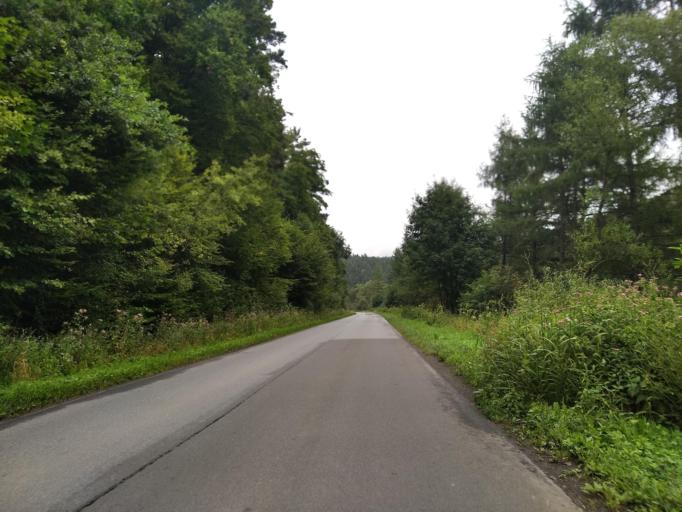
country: PL
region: Subcarpathian Voivodeship
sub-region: Powiat przemyski
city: Bircza
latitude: 49.6844
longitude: 22.4148
